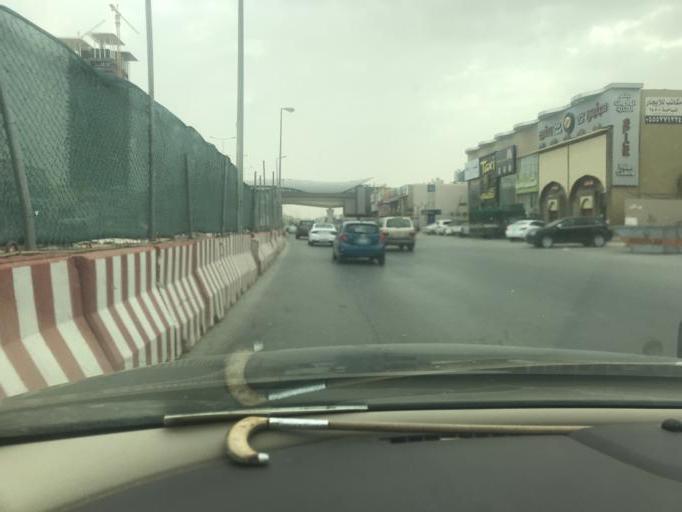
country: SA
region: Ar Riyad
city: Riyadh
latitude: 24.8129
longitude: 46.6283
